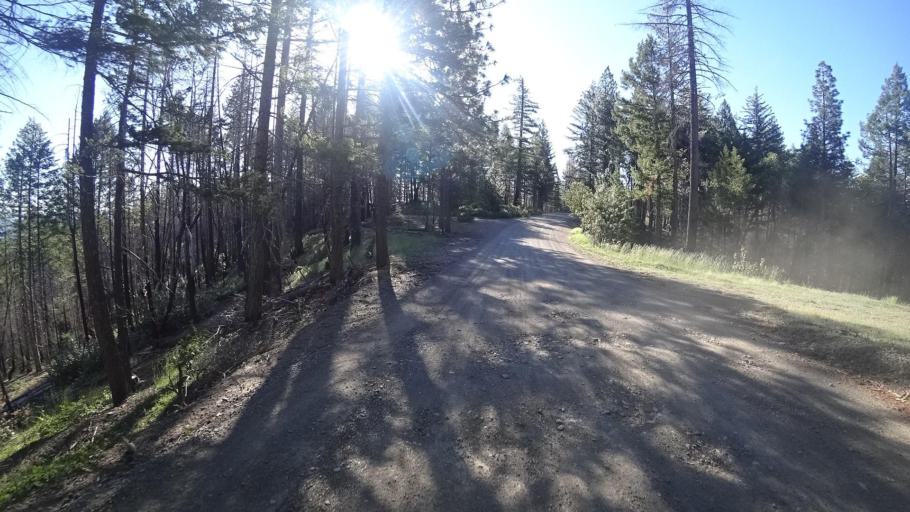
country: US
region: California
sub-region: Lake County
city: Upper Lake
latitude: 39.3578
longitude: -122.9843
